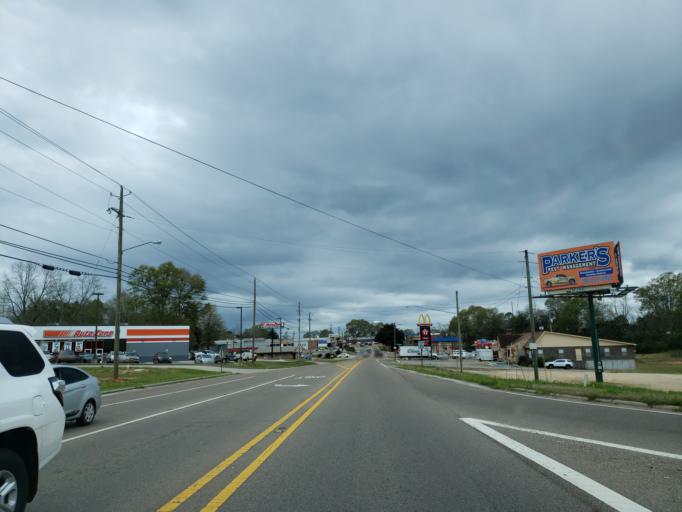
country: US
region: Mississippi
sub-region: Lamar County
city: Purvis
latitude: 31.1463
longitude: -89.4030
